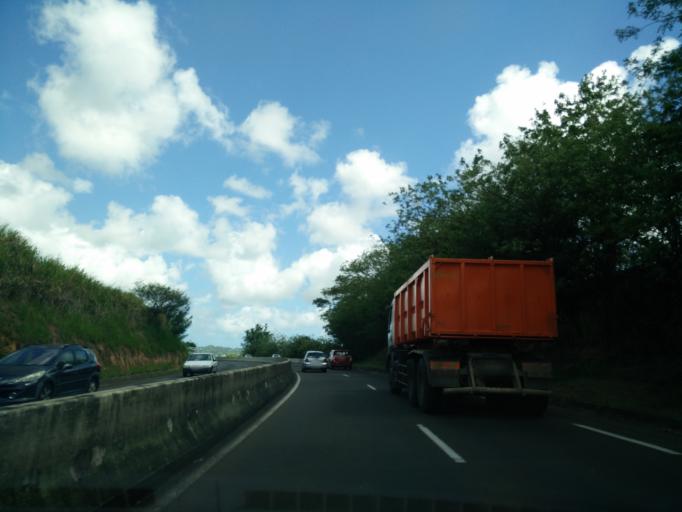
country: MQ
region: Martinique
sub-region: Martinique
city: Ducos
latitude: 14.5636
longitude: -60.9788
